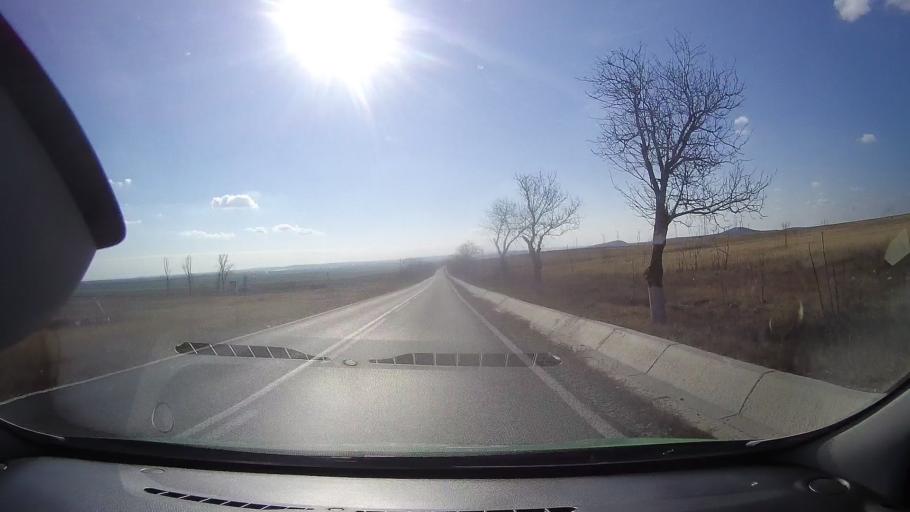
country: RO
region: Tulcea
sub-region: Comuna Ceamurlia de Jos
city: Ceamurlia de Jos
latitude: 44.8124
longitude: 28.6915
